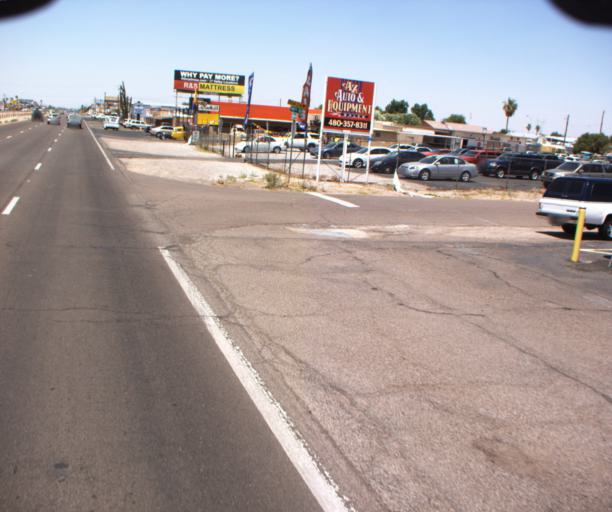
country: US
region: Arizona
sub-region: Pinal County
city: Apache Junction
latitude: 33.4154
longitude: -111.6189
